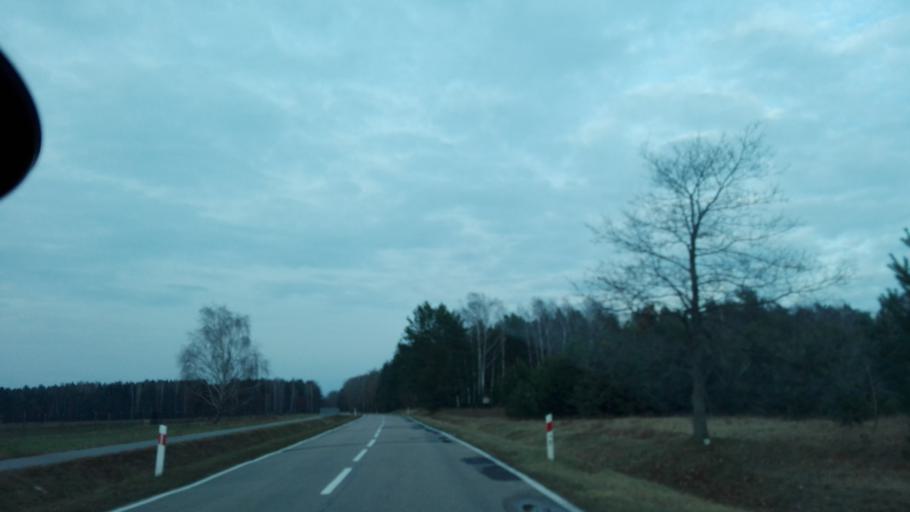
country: PL
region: Lublin Voivodeship
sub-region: Powiat bialski
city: Slawatycze
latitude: 51.7003
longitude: 23.5013
